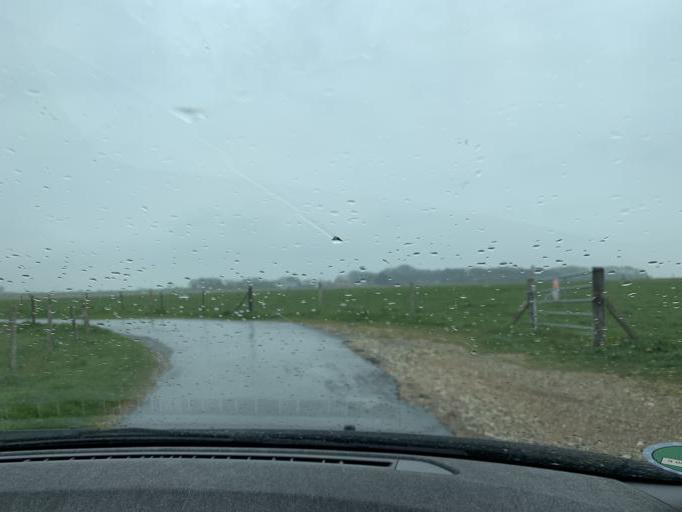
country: FR
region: Haute-Normandie
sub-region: Departement de la Seine-Maritime
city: Saint-Jouin-Bruneval
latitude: 49.6802
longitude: 0.1645
